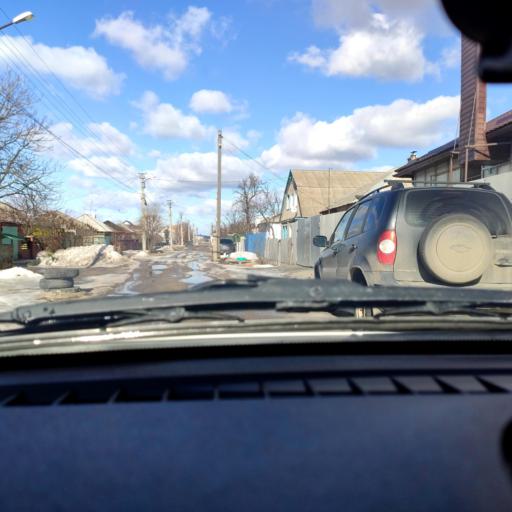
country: RU
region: Voronezj
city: Pridonskoy
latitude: 51.6871
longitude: 39.0579
